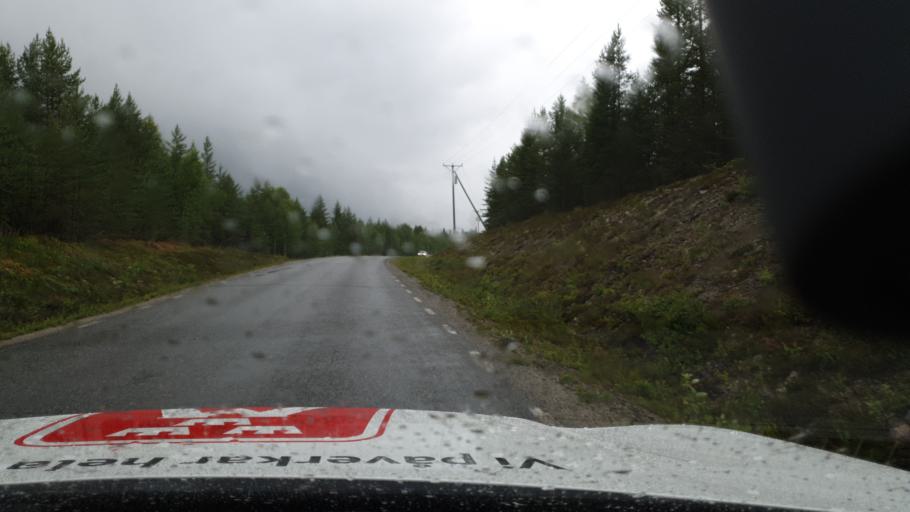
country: SE
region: Vaesterbotten
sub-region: Vindelns Kommun
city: Vindeln
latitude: 64.3997
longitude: 19.6634
